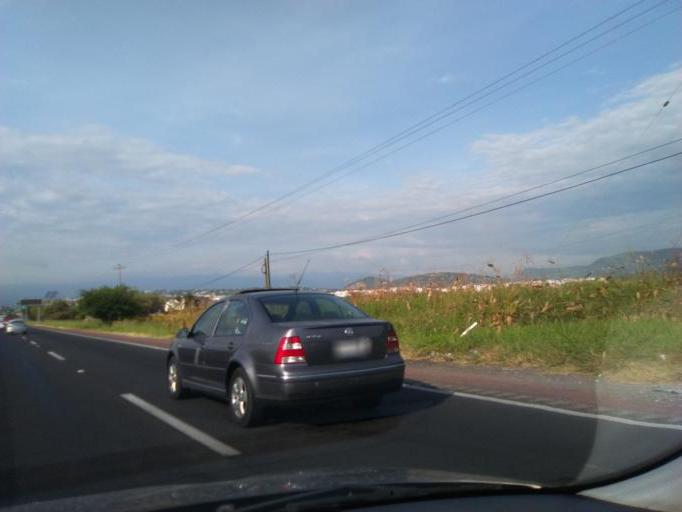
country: MX
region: Morelos
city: Temixco
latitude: 18.8211
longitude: -99.2187
